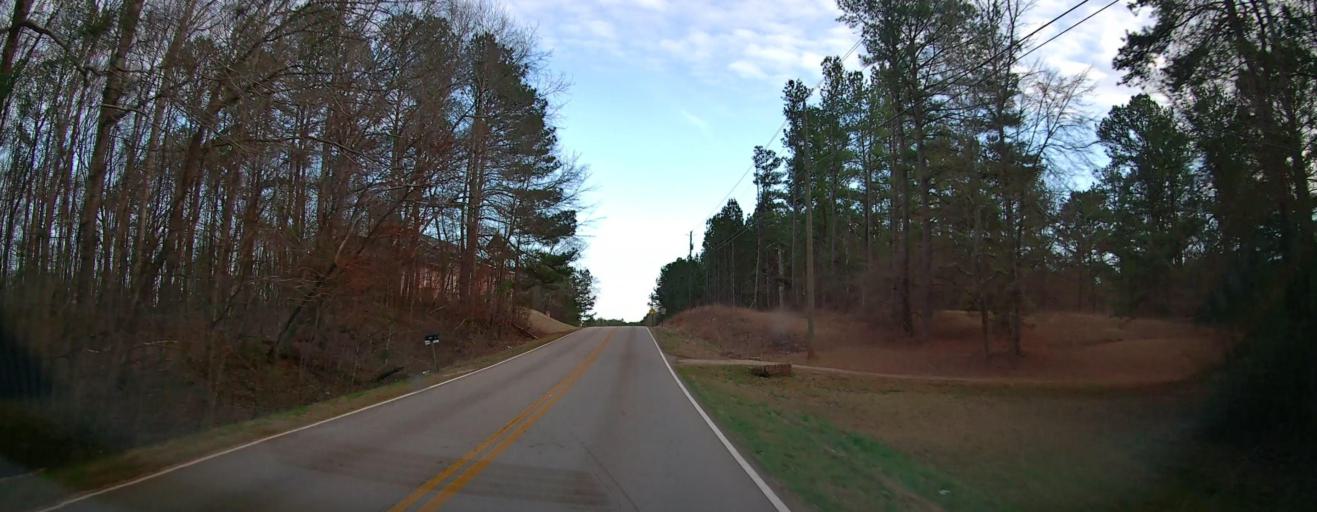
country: US
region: Georgia
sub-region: Troup County
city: West Point
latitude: 32.9436
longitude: -85.1322
